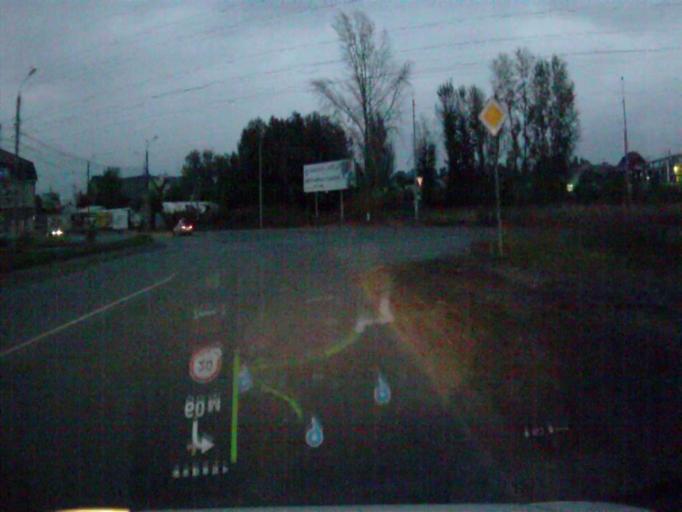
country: RU
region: Chelyabinsk
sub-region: Gorod Chelyabinsk
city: Chelyabinsk
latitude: 55.1570
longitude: 61.2986
